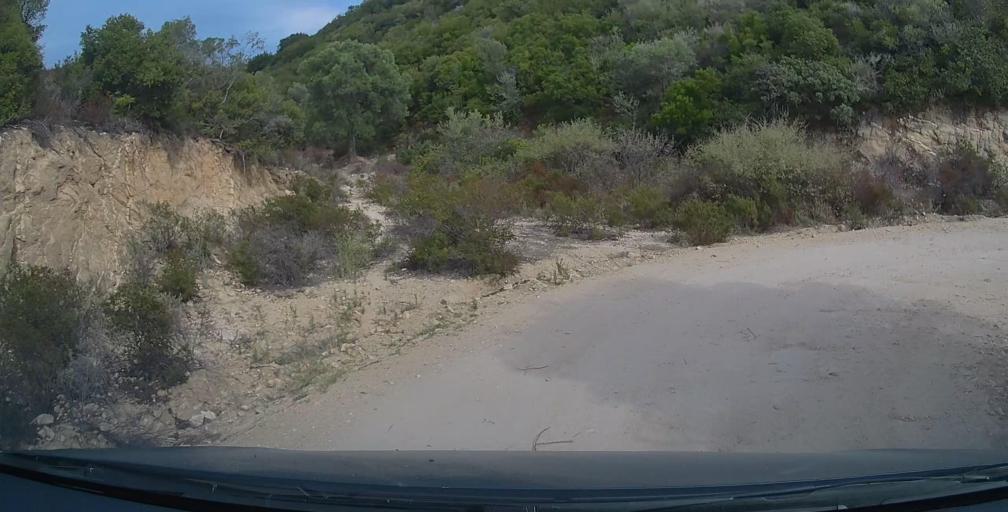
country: GR
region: Central Macedonia
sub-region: Nomos Chalkidikis
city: Sykia
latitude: 39.9913
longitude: 23.9165
